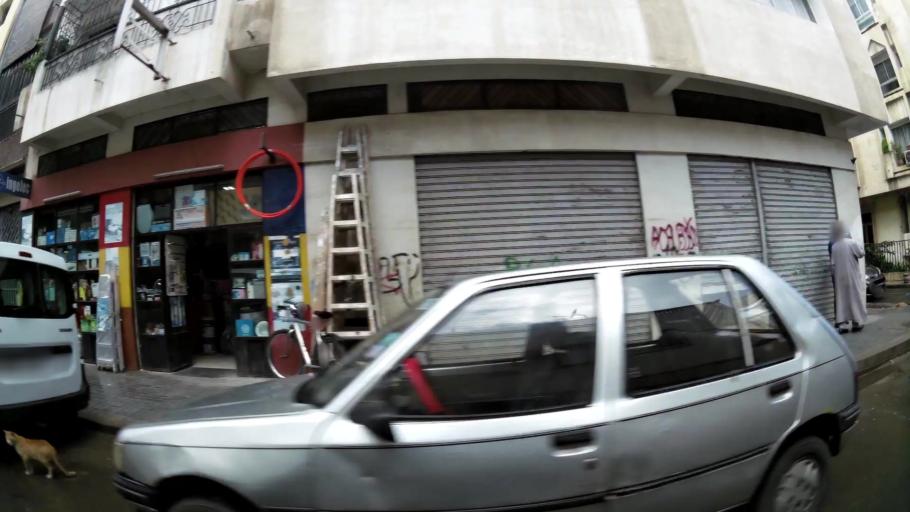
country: MA
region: Grand Casablanca
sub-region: Casablanca
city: Casablanca
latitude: 33.5837
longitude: -7.6168
